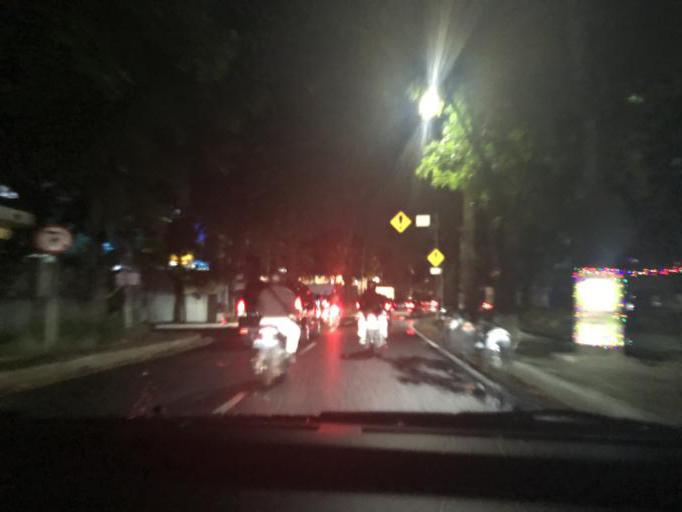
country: ID
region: West Java
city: Bandung
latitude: -6.9080
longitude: 107.6302
